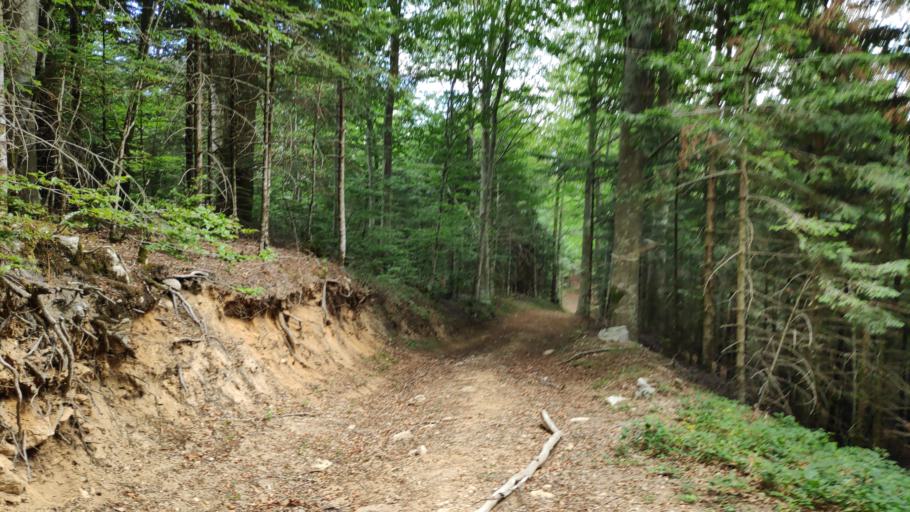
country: IT
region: Calabria
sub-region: Provincia di Vibo-Valentia
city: Serra San Bruno
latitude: 38.5444
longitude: 16.3647
